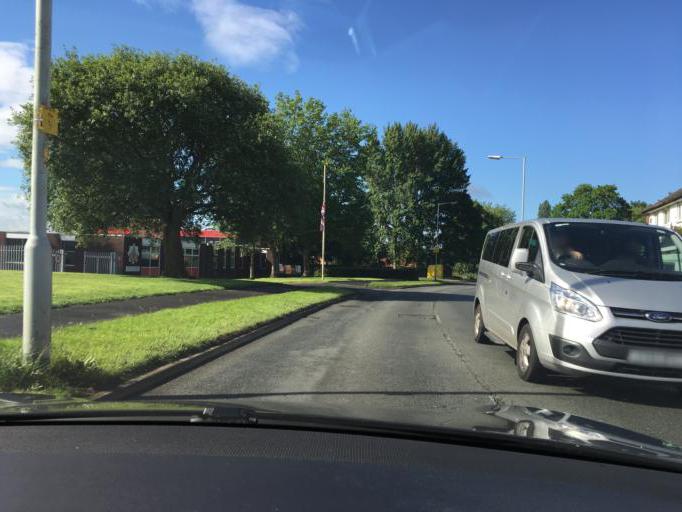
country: GB
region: England
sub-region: Borough of Stockport
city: Hazel Grove
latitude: 53.3945
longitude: -2.1248
